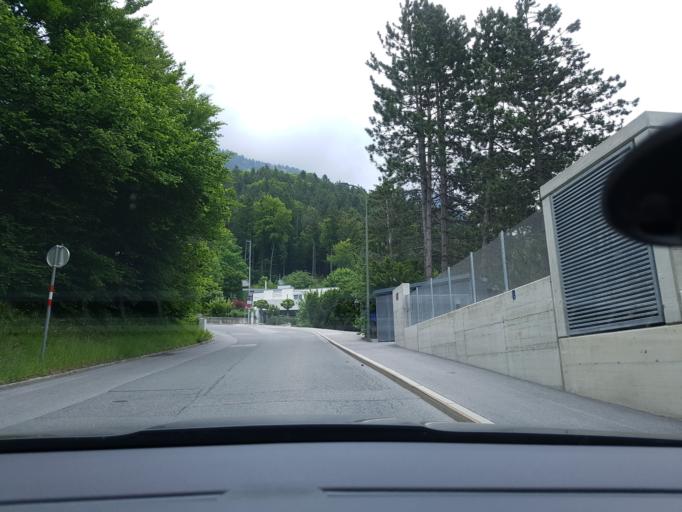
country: AT
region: Tyrol
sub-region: Politischer Bezirk Innsbruck Land
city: Vols
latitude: 47.2672
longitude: 11.3303
